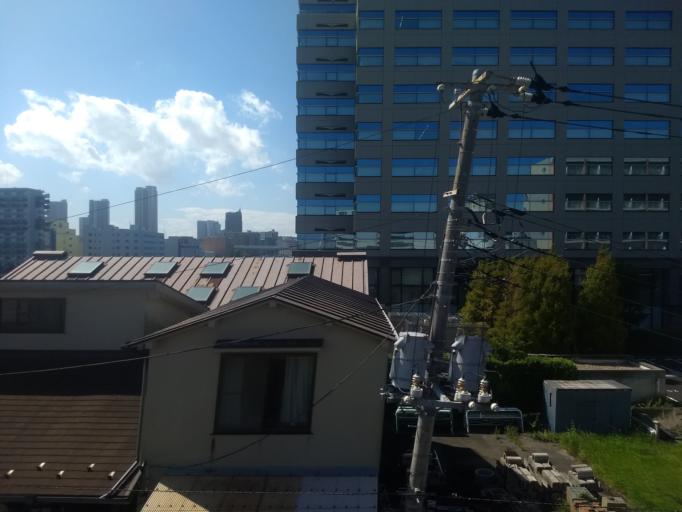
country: JP
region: Tokyo
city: Urayasu
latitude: 35.6555
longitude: 139.8192
